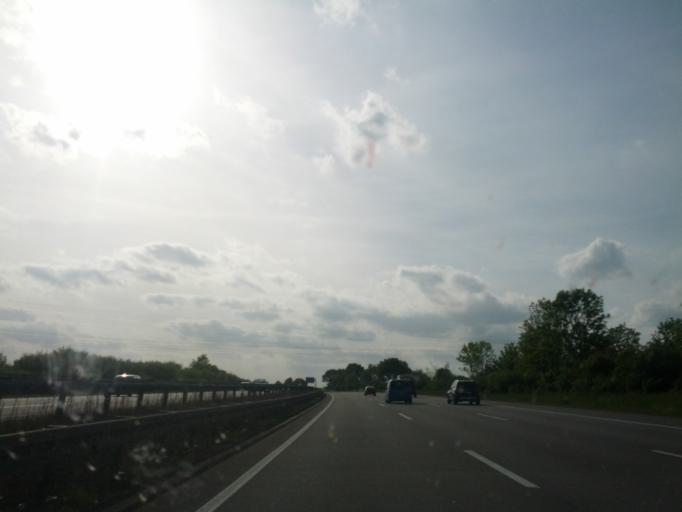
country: DE
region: Thuringia
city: Schwabhausen
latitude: 50.9004
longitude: 10.7429
